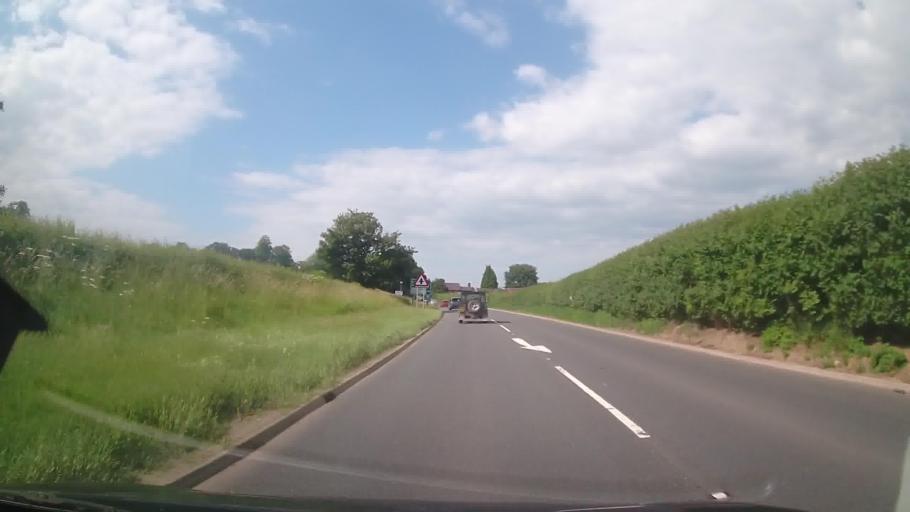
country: GB
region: England
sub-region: Shropshire
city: Ludlow
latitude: 52.3324
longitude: -2.7123
